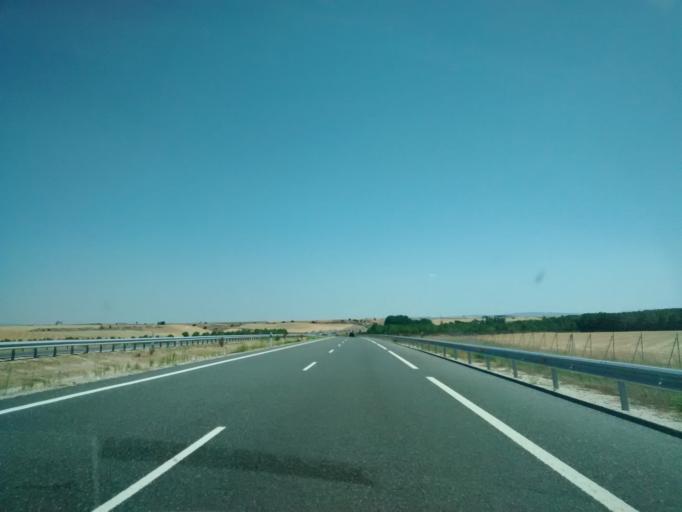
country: ES
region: Castille and Leon
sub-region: Provincia de Avila
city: Rivilla de Barajas
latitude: 40.8814
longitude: -4.9988
